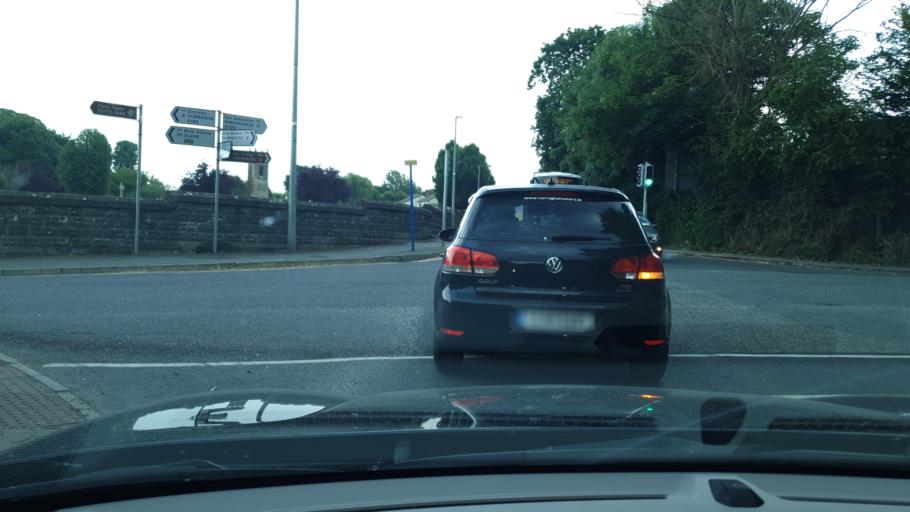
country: IE
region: Leinster
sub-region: An Mhi
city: Ratoath
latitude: 53.5093
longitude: -6.4626
